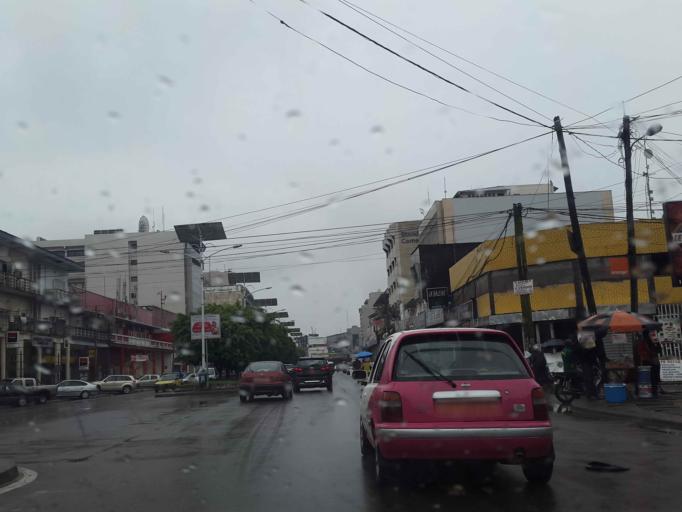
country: CM
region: Littoral
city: Douala
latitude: 4.0528
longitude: 9.6972
